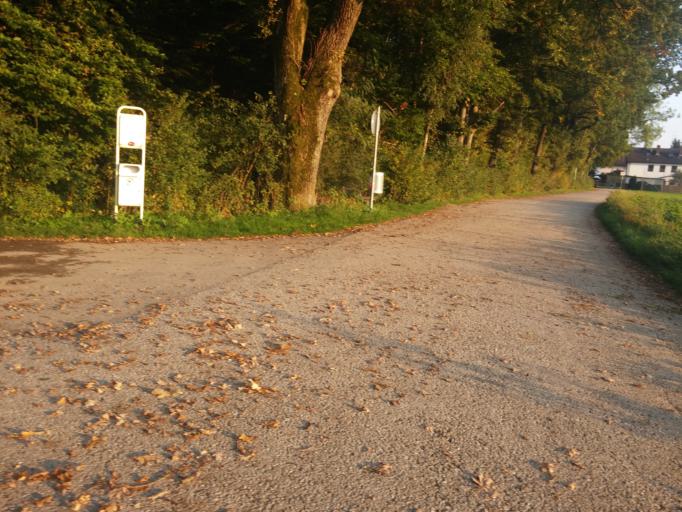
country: DE
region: Bavaria
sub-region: Upper Bavaria
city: Zorneding
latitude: 48.0965
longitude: 11.8408
